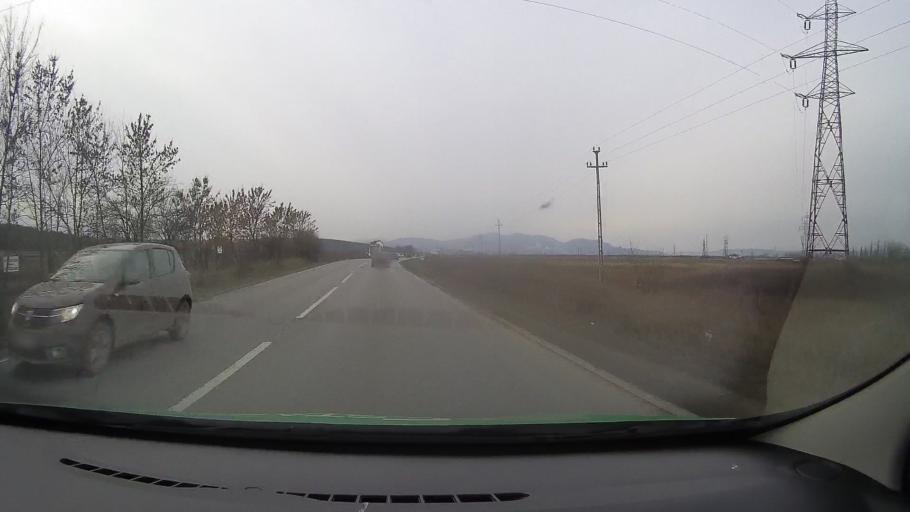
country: RO
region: Hunedoara
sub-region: Oras Simeria
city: Simeria
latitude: 45.8478
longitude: 23.0021
